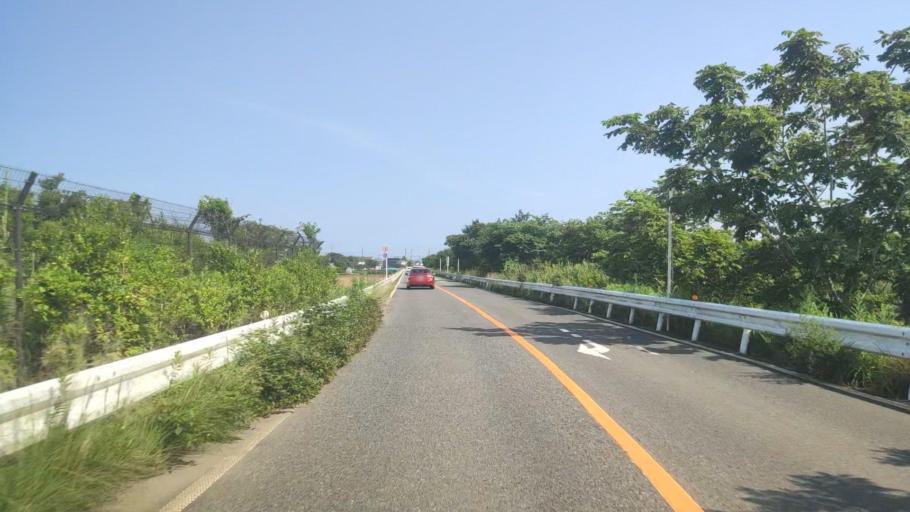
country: JP
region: Kanagawa
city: Isehara
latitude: 35.3644
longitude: 139.3210
